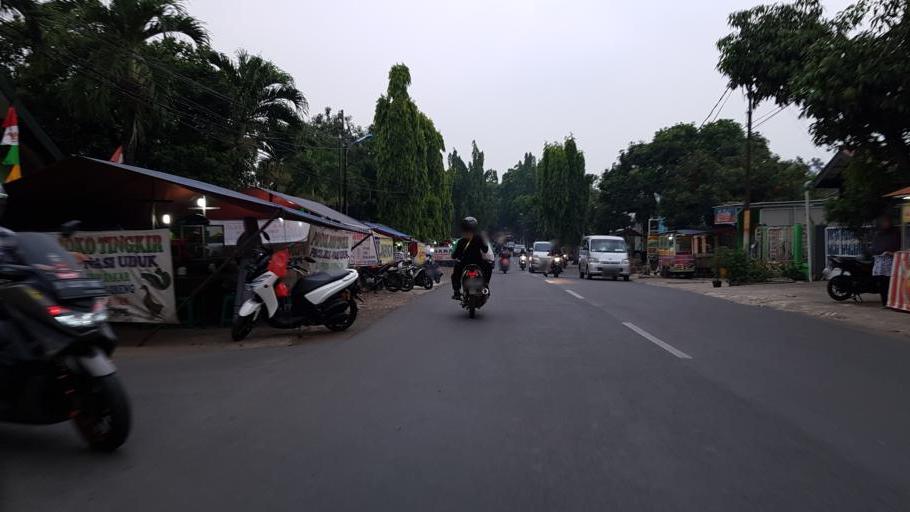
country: ID
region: West Java
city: Depok
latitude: -6.3319
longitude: 106.8458
